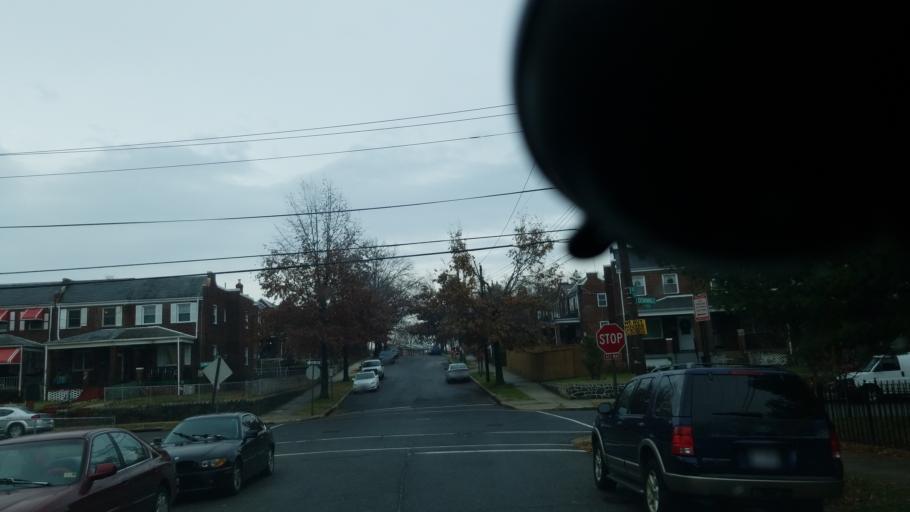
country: US
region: Maryland
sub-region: Prince George's County
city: Mount Rainier
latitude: 38.9216
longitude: -76.9848
